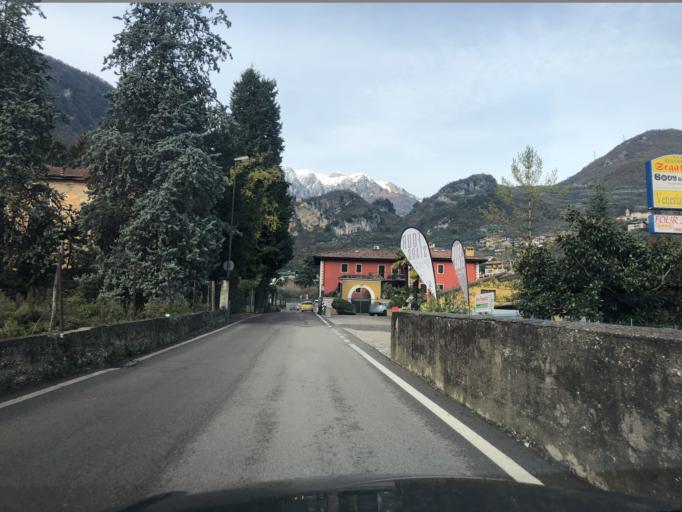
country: IT
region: Trentino-Alto Adige
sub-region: Provincia di Trento
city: Tenno
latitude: 45.9074
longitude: 10.8477
